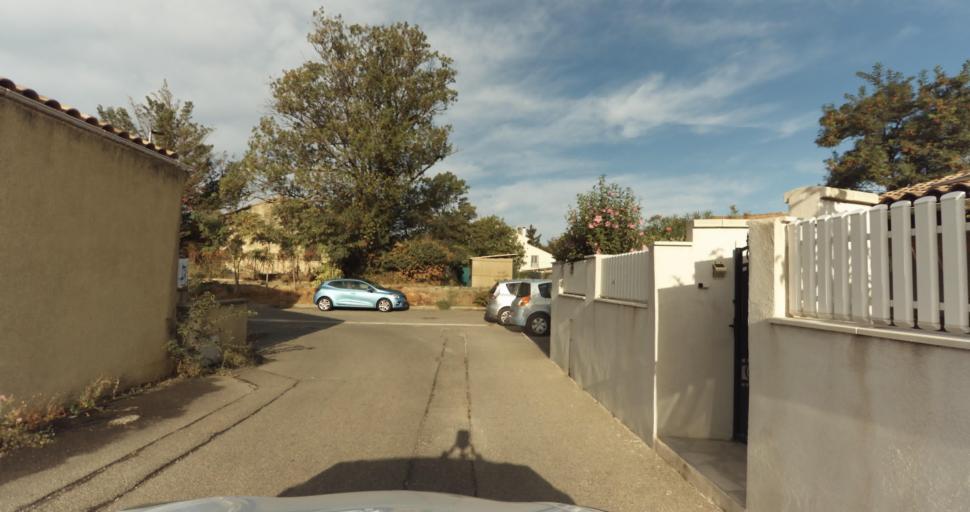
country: FR
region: Provence-Alpes-Cote d'Azur
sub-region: Departement des Bouches-du-Rhone
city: Miramas
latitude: 43.5819
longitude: 5.0117
